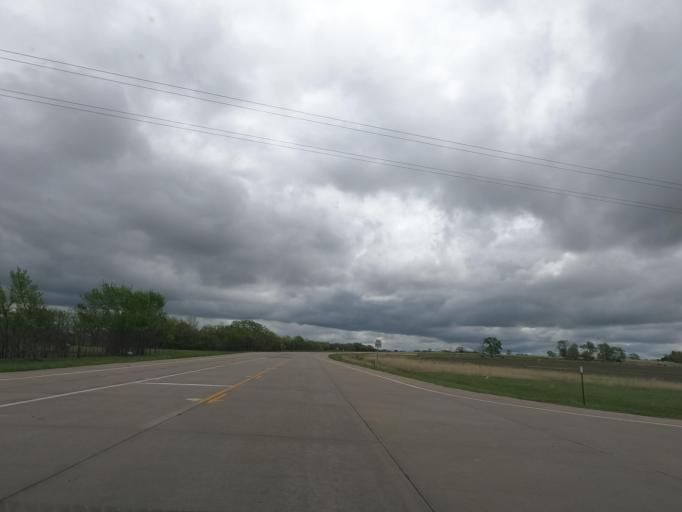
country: US
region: Kansas
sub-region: Wilson County
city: Fredonia
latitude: 37.5508
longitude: -95.8146
